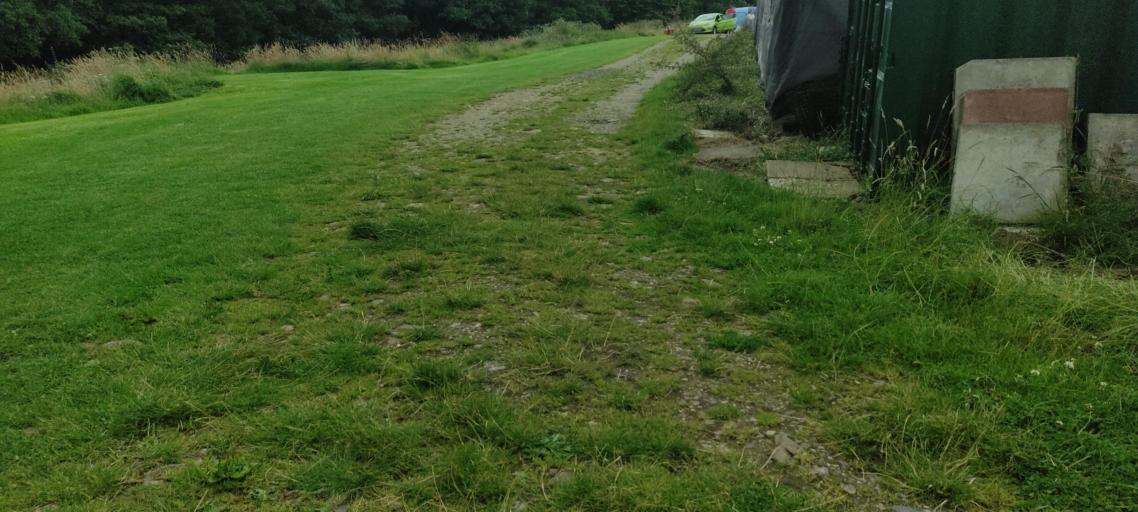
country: GB
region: England
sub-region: Cumbria
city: Wigton
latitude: 54.7501
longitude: -3.0441
